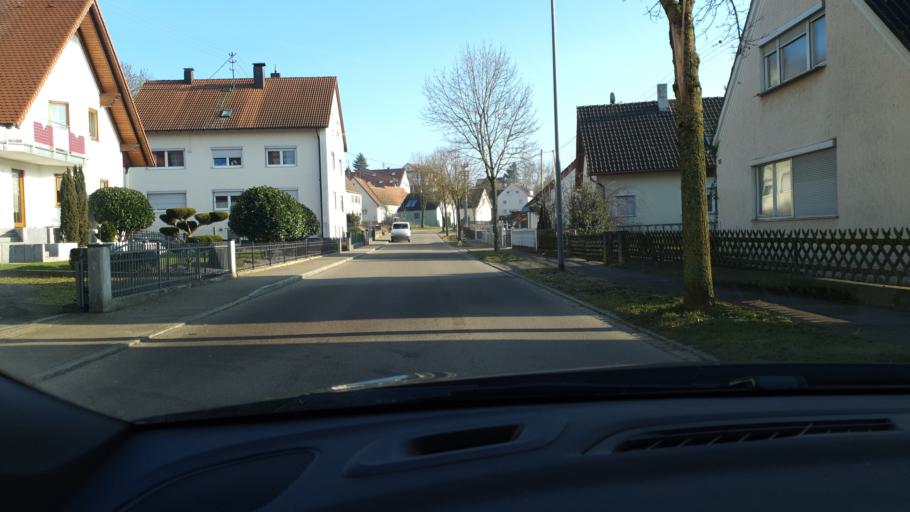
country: DE
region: Bavaria
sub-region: Swabia
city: Burgau
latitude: 48.4325
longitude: 10.3926
